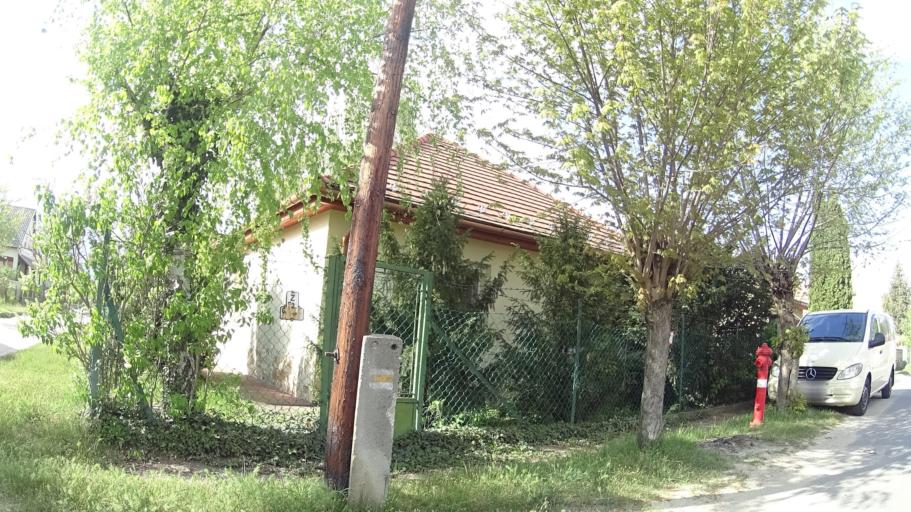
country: HU
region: Pest
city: Veresegyhaz
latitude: 47.6436
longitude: 19.2847
